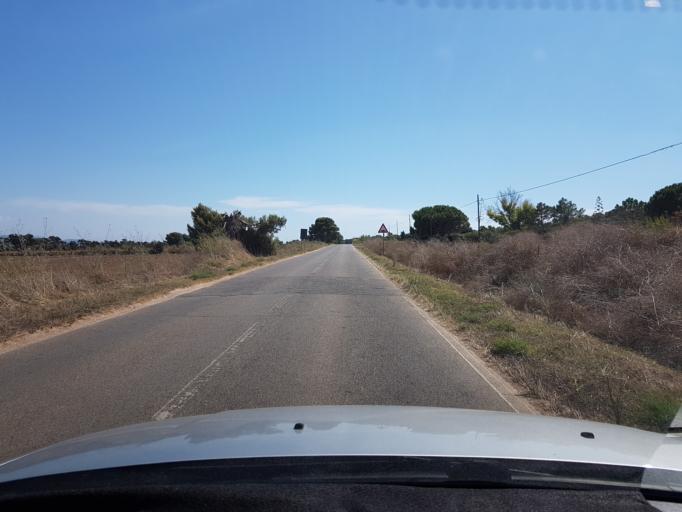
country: IT
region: Sardinia
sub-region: Provincia di Oristano
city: Cabras
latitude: 39.9074
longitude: 8.4380
